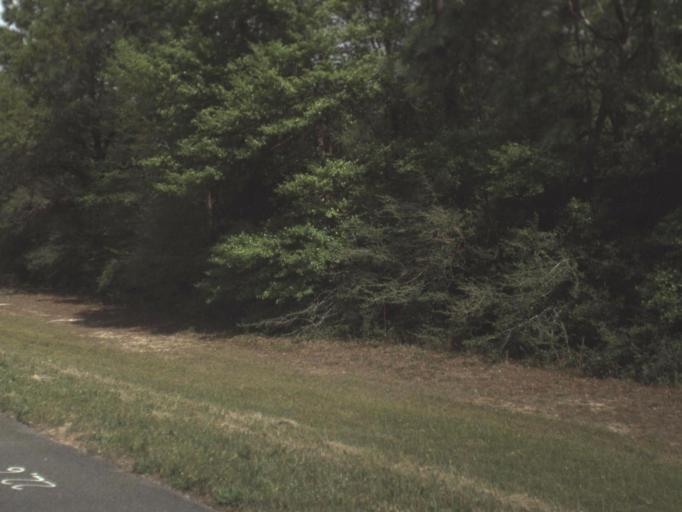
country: US
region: Florida
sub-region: Santa Rosa County
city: East Milton
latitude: 30.6657
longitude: -86.8705
